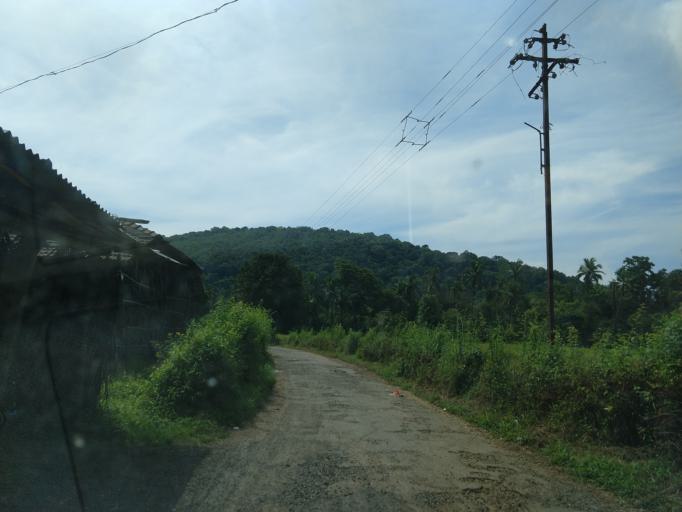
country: IN
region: Maharashtra
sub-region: Sindhudurg
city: Savantvadi
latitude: 15.9752
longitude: 73.7870
